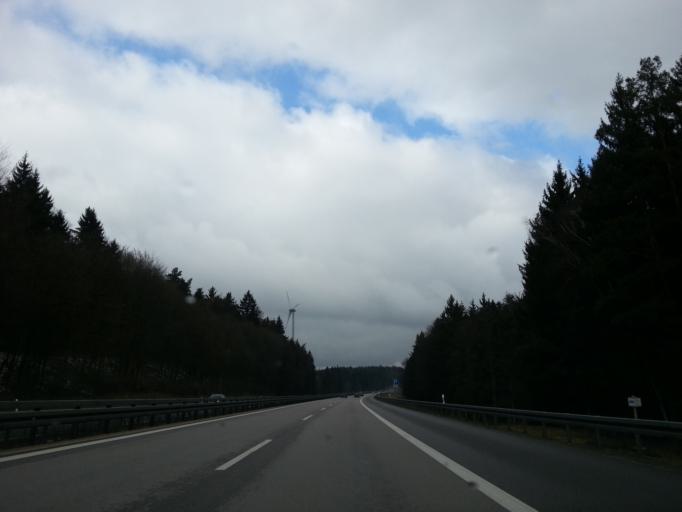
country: DE
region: Bavaria
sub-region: Upper Palatinate
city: Brunn
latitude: 49.1098
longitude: 11.8767
